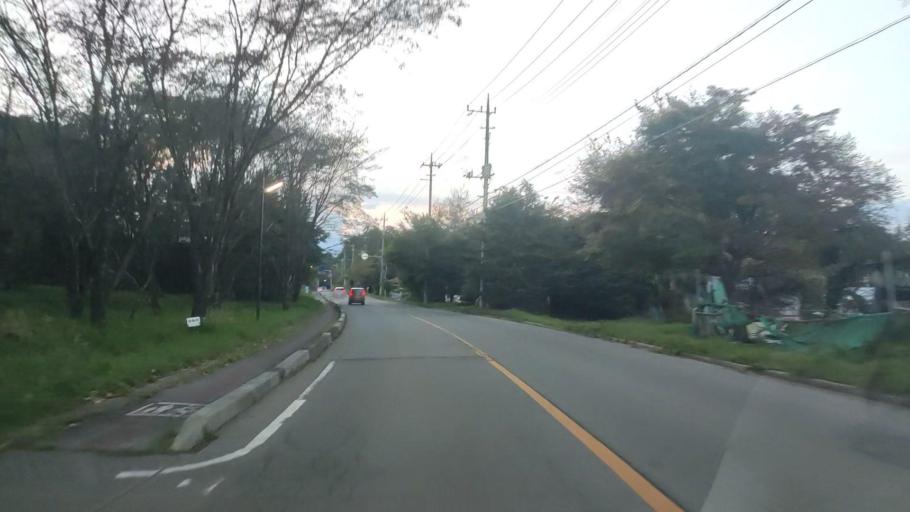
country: JP
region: Nagano
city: Komoro
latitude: 36.4846
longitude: 138.5850
